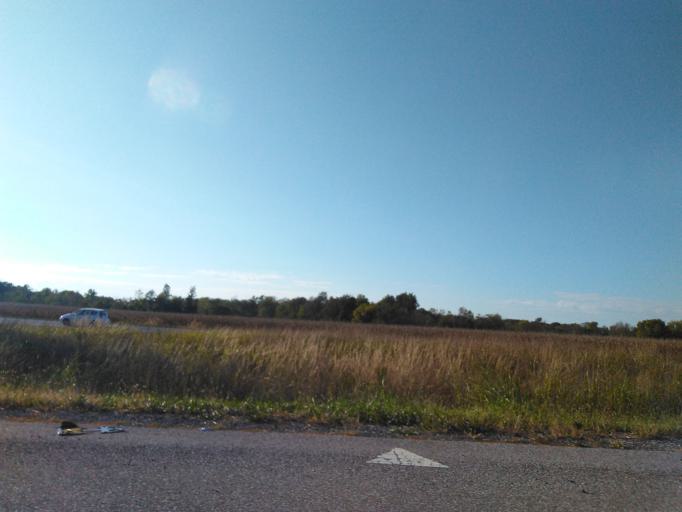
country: US
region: Illinois
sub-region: Madison County
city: Maryville
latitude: 38.7186
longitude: -89.9213
